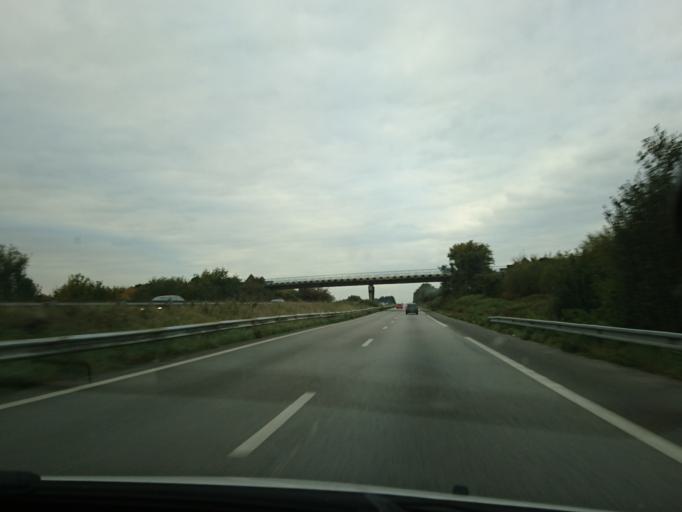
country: FR
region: Brittany
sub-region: Departement du Morbihan
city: Brech
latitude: 47.7056
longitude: -3.0466
